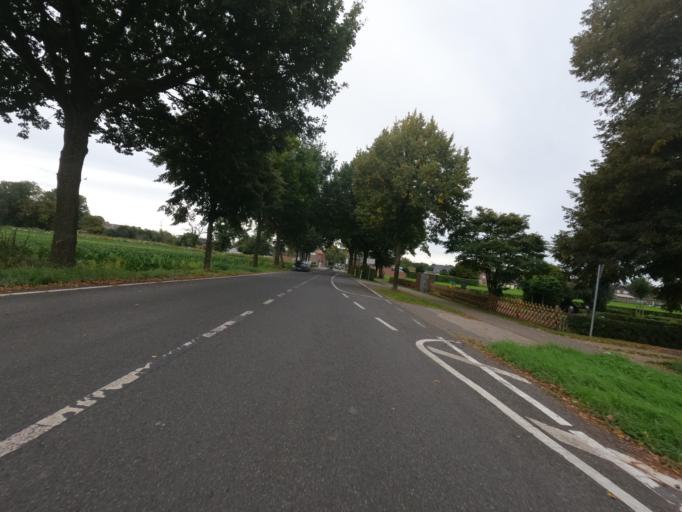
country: DE
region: North Rhine-Westphalia
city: Baesweiler
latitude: 50.9391
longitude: 6.2023
